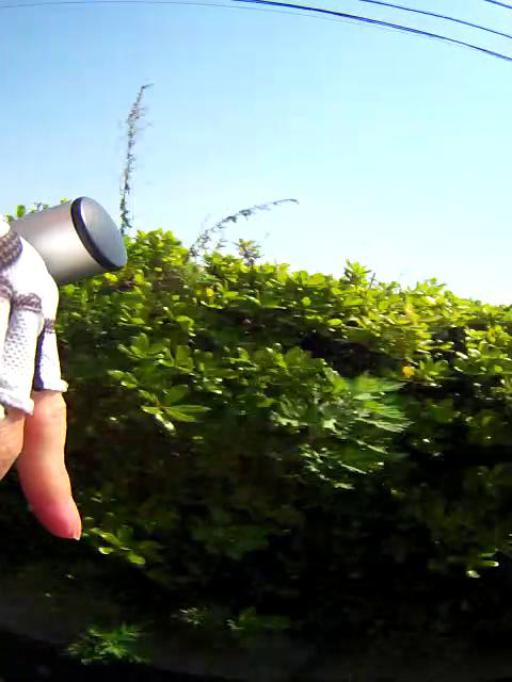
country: JP
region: Osaka
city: Matsubara
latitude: 34.5523
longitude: 135.5532
